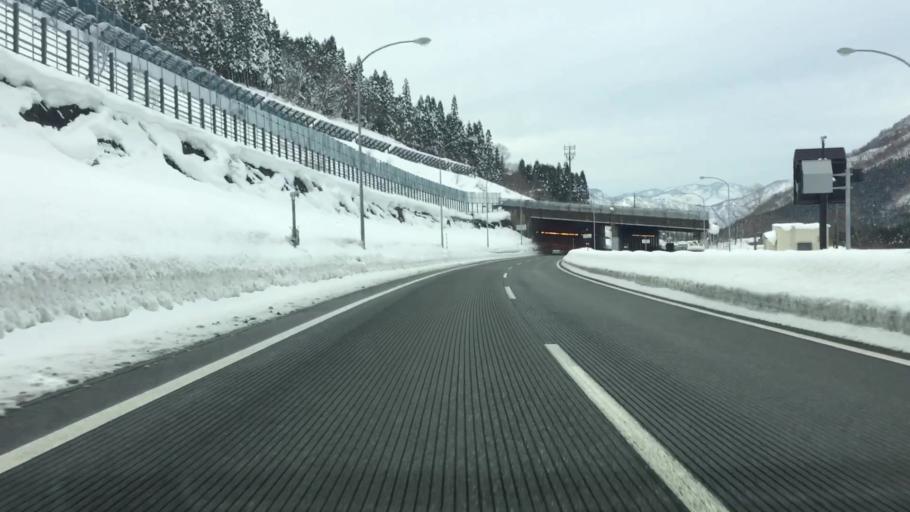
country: JP
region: Niigata
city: Shiozawa
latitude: 36.8690
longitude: 138.8667
